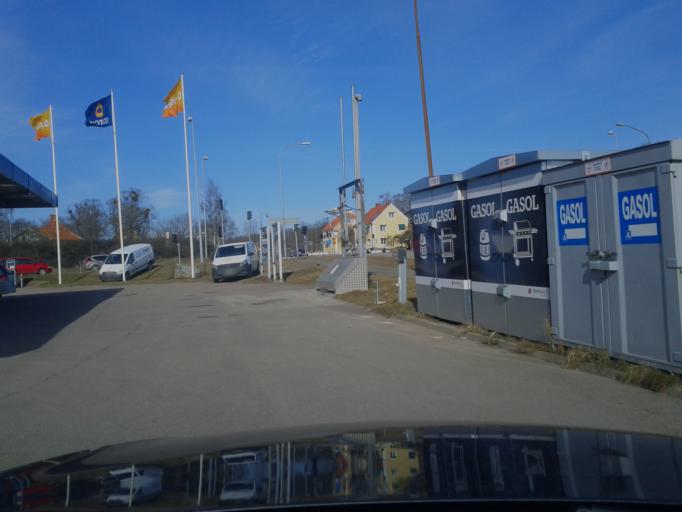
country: SE
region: Vaestmanland
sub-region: Vasteras
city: Vasteras
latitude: 59.6145
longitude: 16.5765
